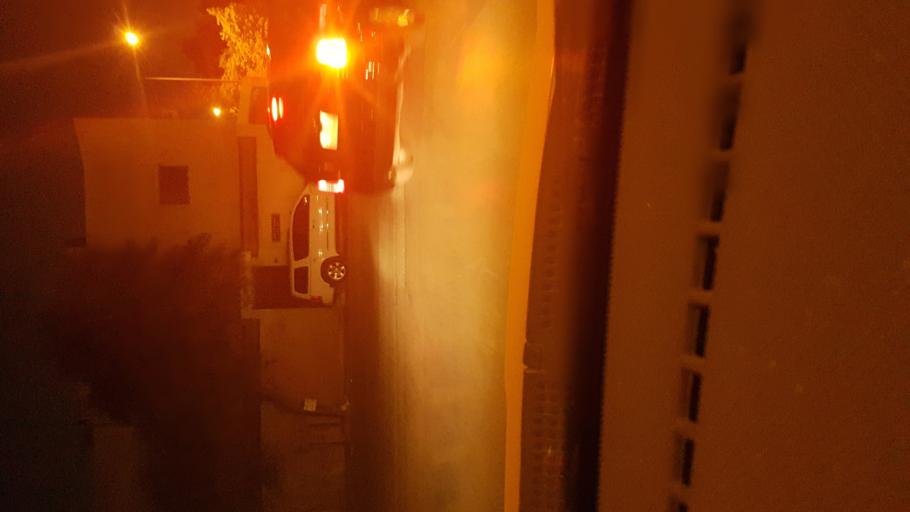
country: SA
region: Ar Riyad
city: Riyadh
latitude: 24.6907
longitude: 46.6918
